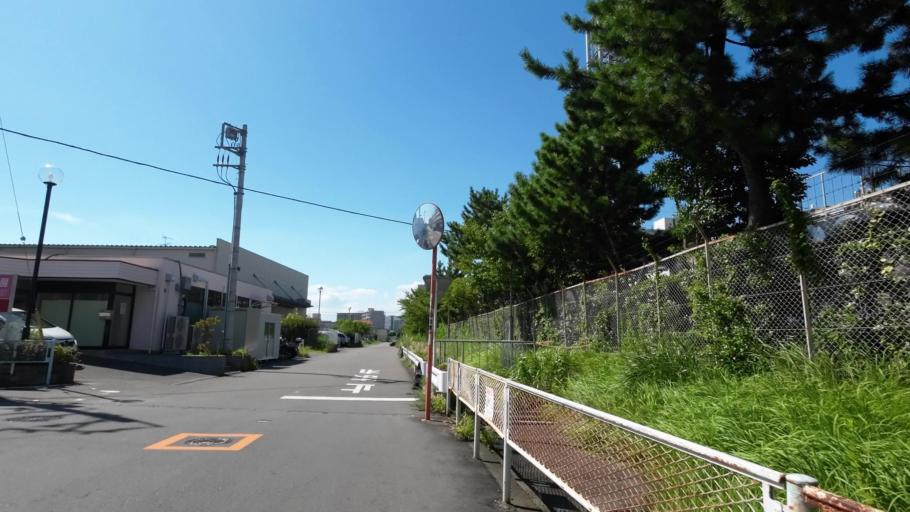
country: JP
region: Kanagawa
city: Kamakura
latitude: 35.3389
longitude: 139.5205
